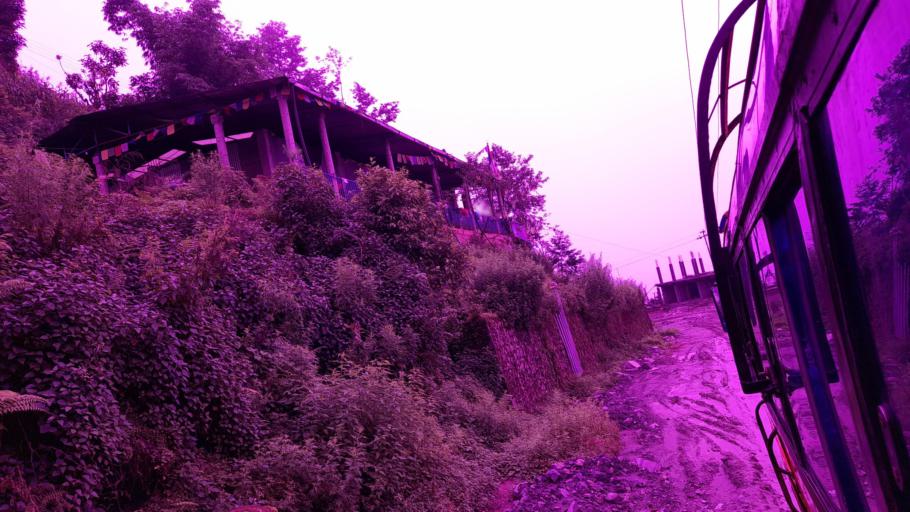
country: NP
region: Central Region
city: Kirtipur
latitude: 27.8145
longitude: 85.2203
